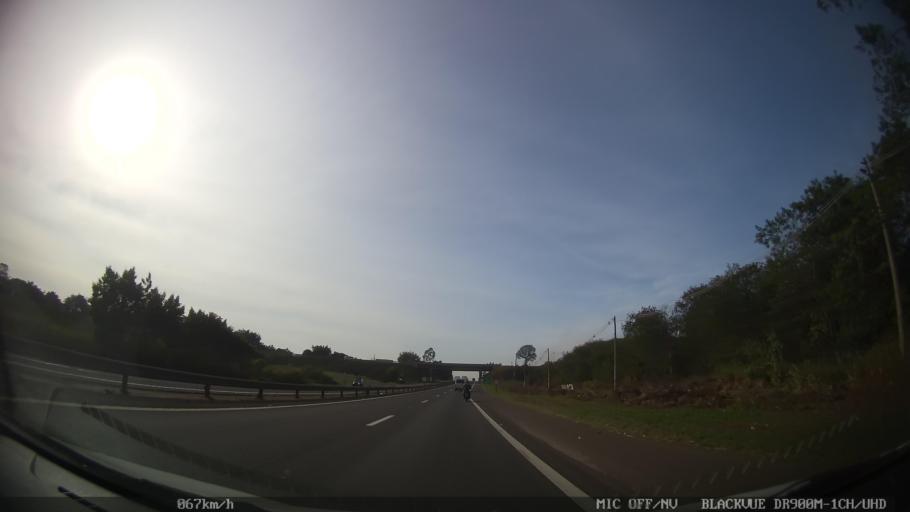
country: BR
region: Sao Paulo
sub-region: Piracicaba
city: Piracicaba
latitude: -22.6829
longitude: -47.6883
